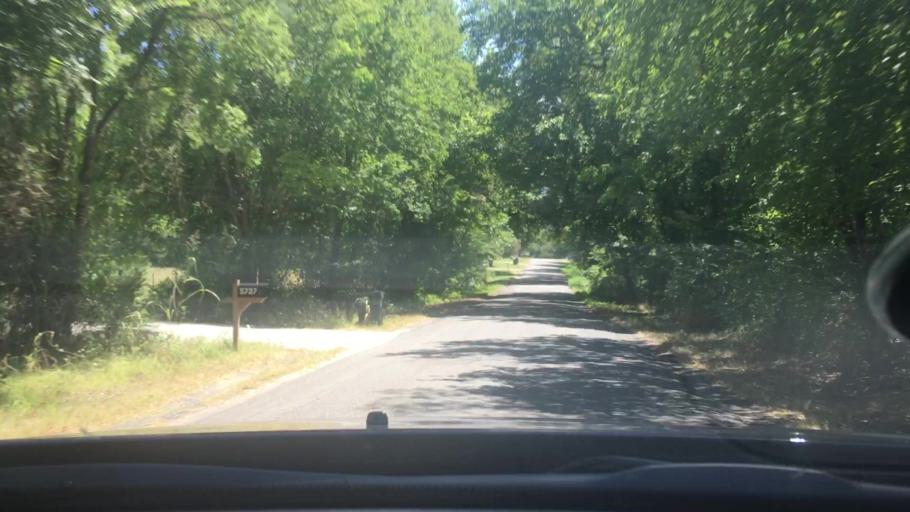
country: US
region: Oklahoma
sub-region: Bryan County
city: Durant
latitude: 33.9830
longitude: -96.2579
